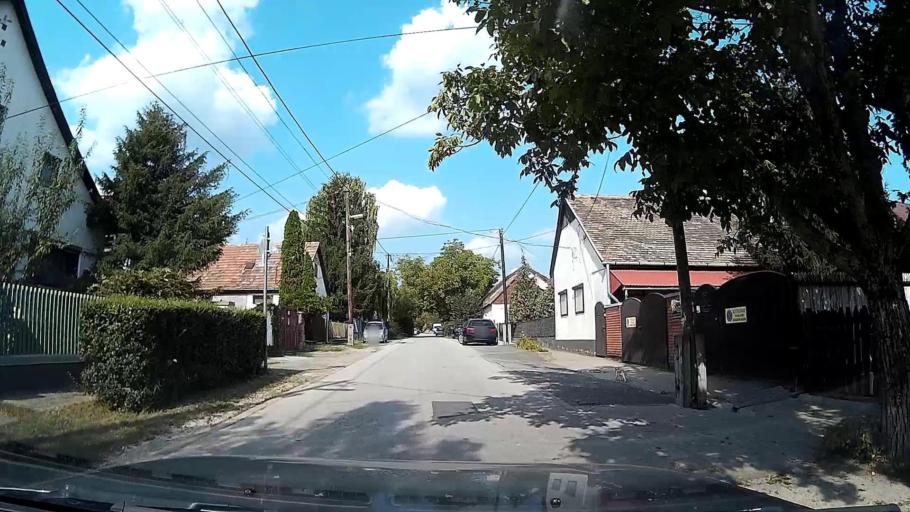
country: HU
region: Pest
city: Budakeszi
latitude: 47.5094
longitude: 18.9220
